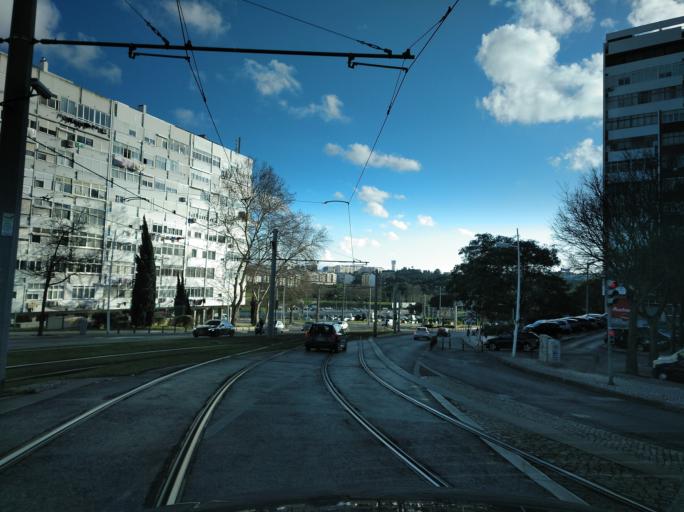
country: PT
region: Setubal
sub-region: Almada
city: Pragal
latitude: 38.6692
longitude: -9.1659
